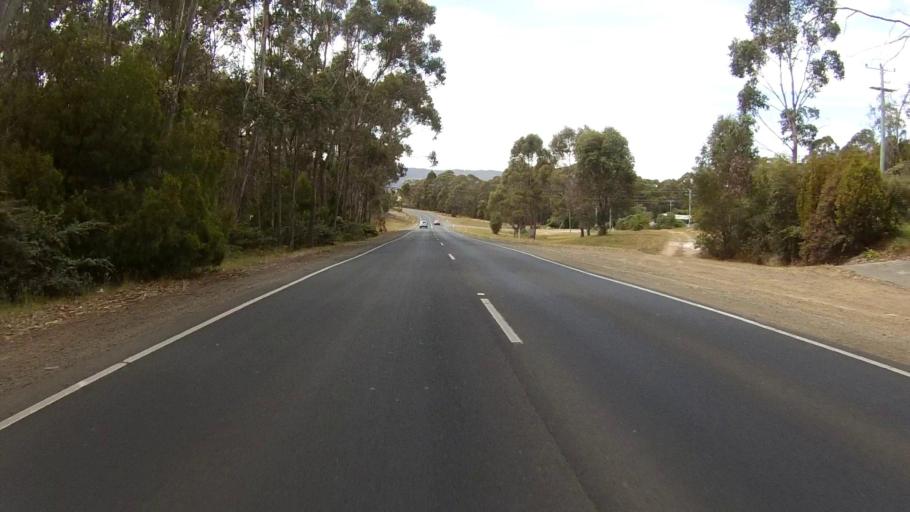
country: AU
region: Tasmania
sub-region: Kingborough
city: Margate
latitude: -43.0559
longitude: 147.2579
